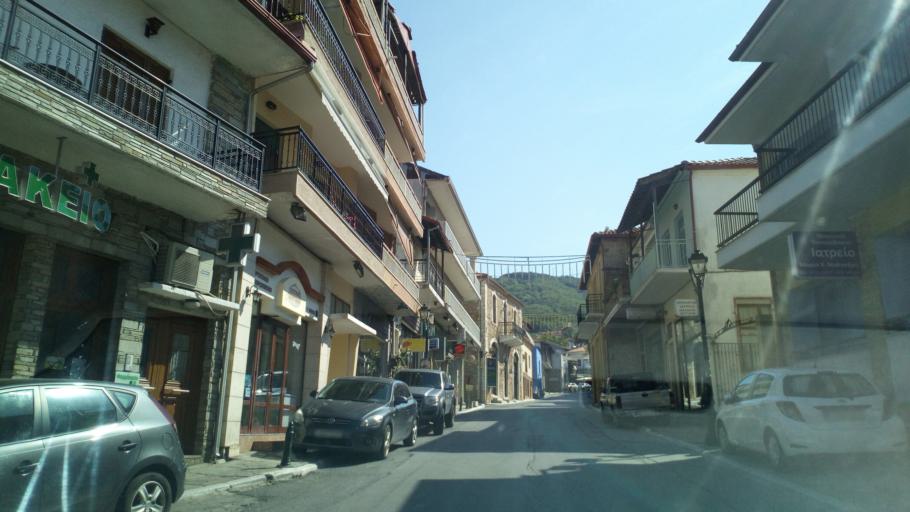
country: GR
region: Central Macedonia
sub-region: Nomos Chalkidikis
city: Arnaia
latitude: 40.4875
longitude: 23.5960
